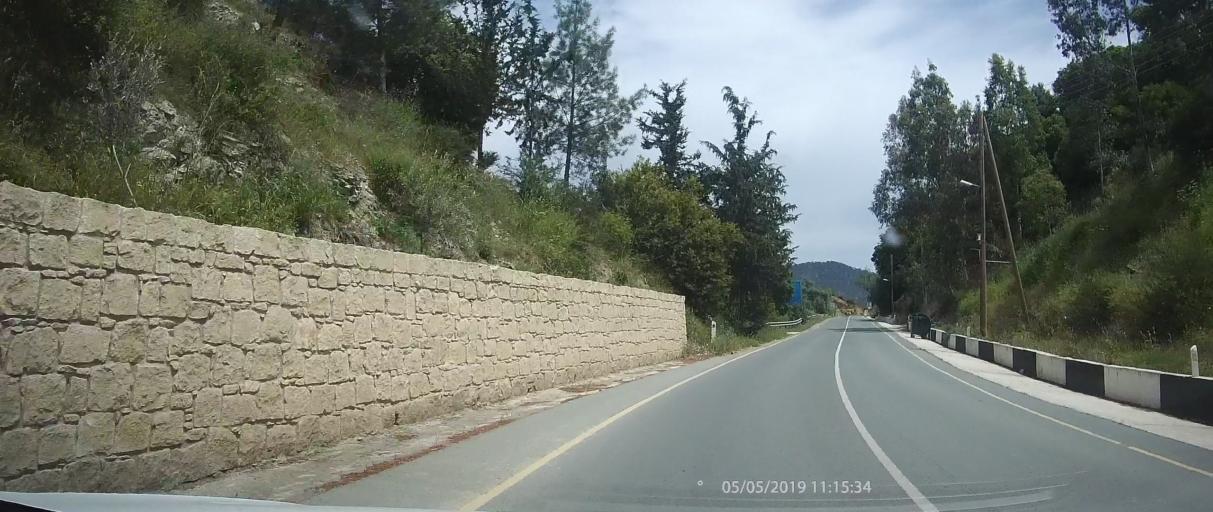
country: CY
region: Pafos
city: Mesogi
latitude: 34.9192
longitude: 32.5760
